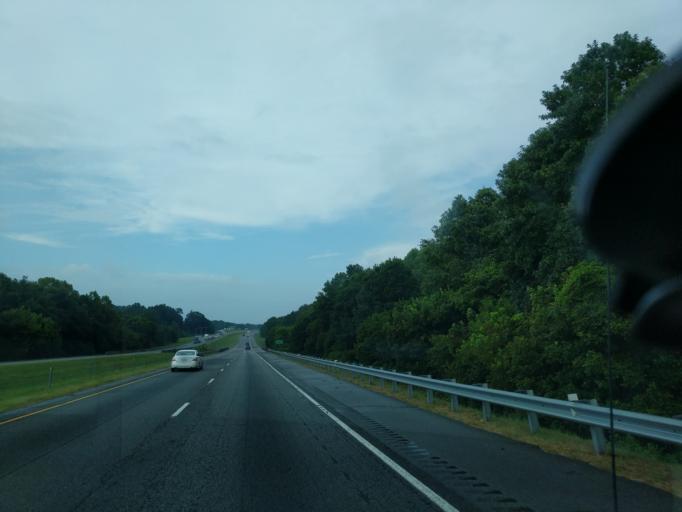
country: US
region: Georgia
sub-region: Franklin County
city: Carnesville
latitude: 34.4101
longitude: -83.1889
